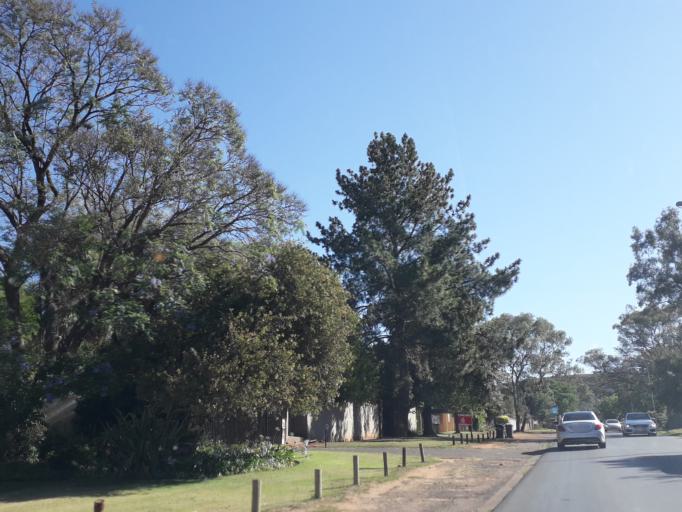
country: ZA
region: Gauteng
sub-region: City of Johannesburg Metropolitan Municipality
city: Roodepoort
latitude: -26.1469
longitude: 27.9518
